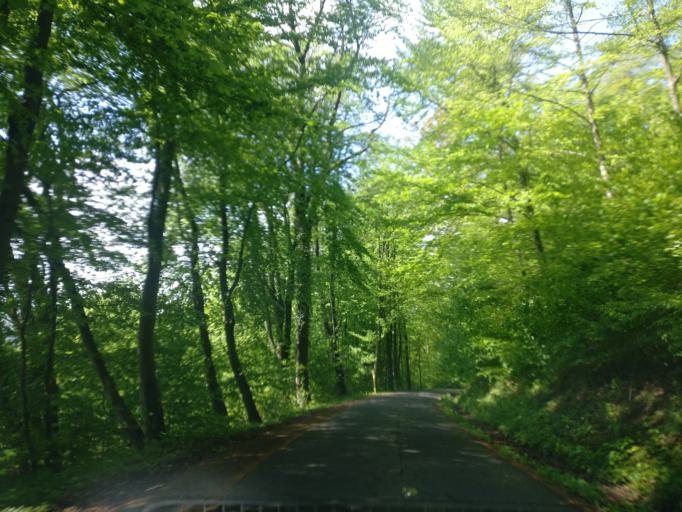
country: DE
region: Lower Saxony
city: Hannoversch Munden
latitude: 51.4484
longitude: 9.6528
